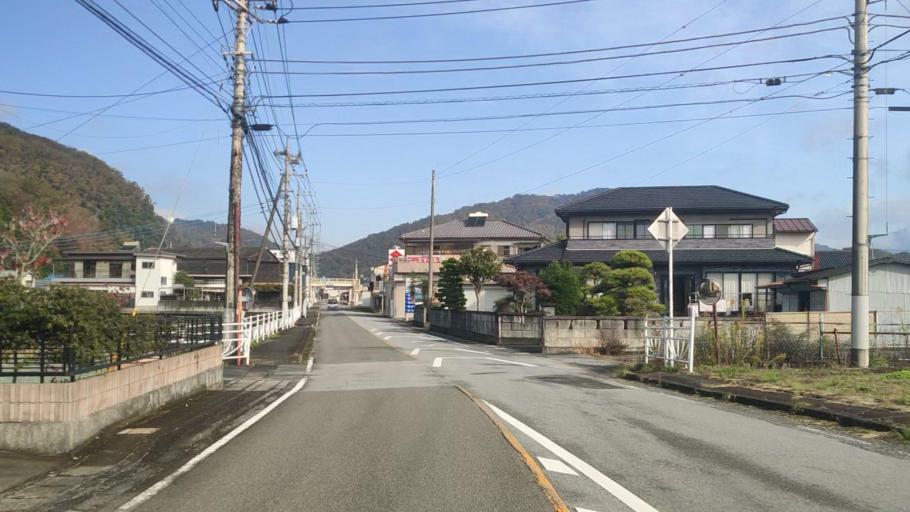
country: JP
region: Yamanashi
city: Ryuo
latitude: 35.4876
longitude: 138.4494
